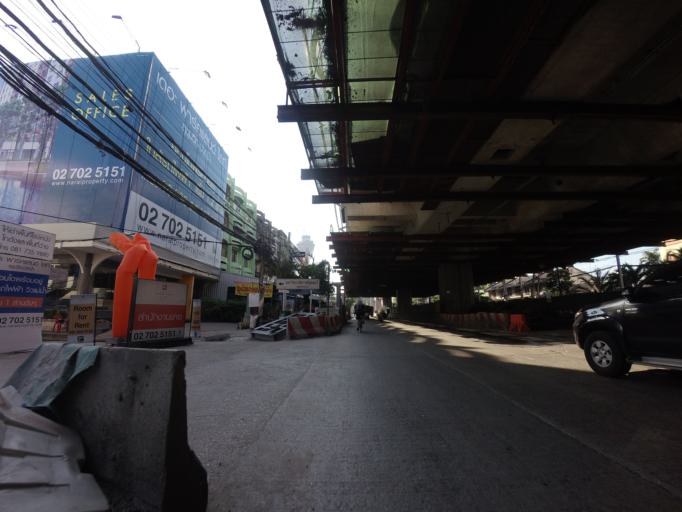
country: TH
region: Samut Prakan
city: Samut Prakan
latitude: 13.6023
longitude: 100.5972
